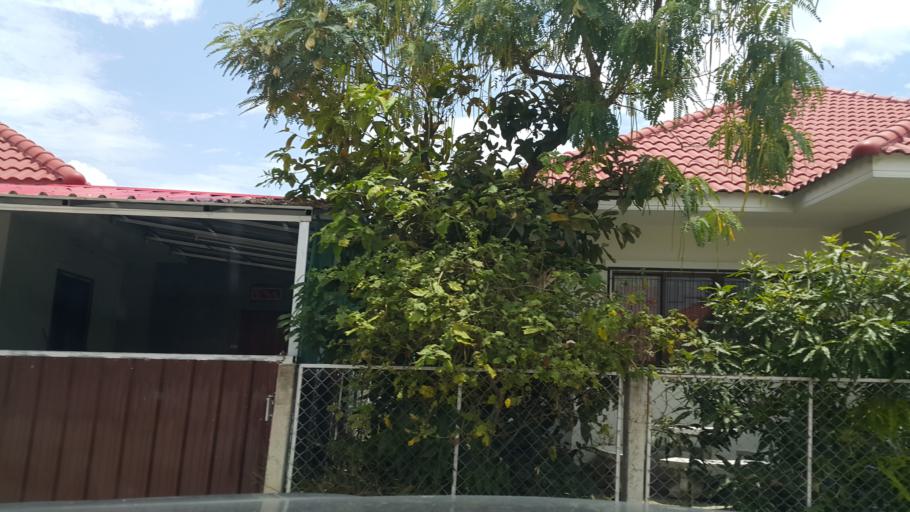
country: TH
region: Chiang Mai
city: Hang Dong
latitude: 18.7056
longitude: 98.9729
